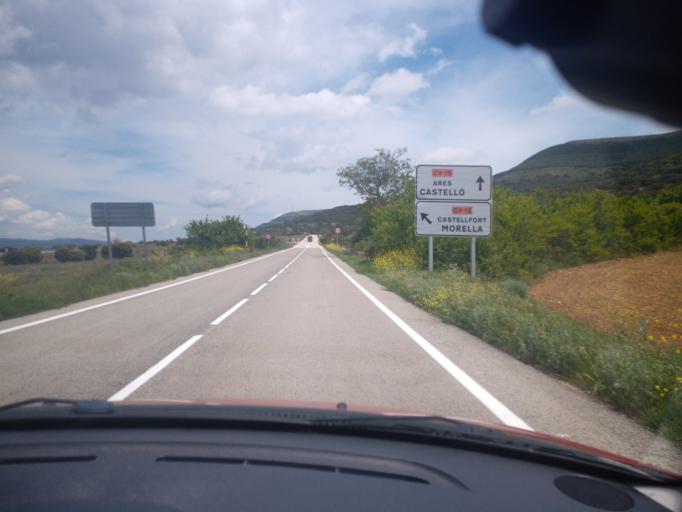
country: ES
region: Valencia
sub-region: Provincia de Castello
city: Ares del Maestre
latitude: 40.4547
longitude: -0.1673
